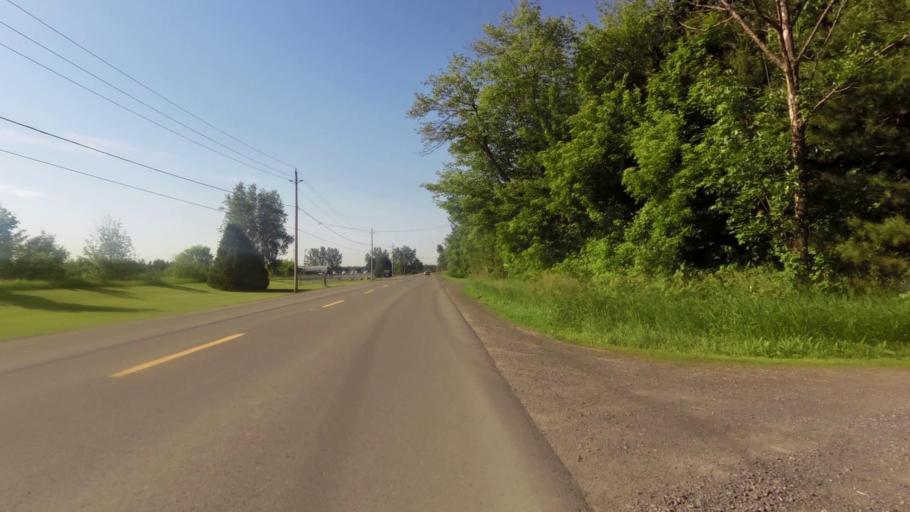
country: CA
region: Ontario
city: Ottawa
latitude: 45.2349
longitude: -75.5611
